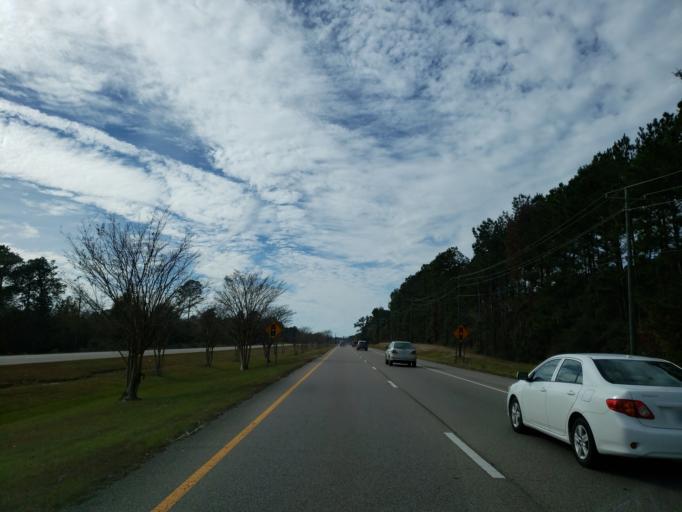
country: US
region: Mississippi
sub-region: Lamar County
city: West Hattiesburg
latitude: 31.3147
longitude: -89.4520
